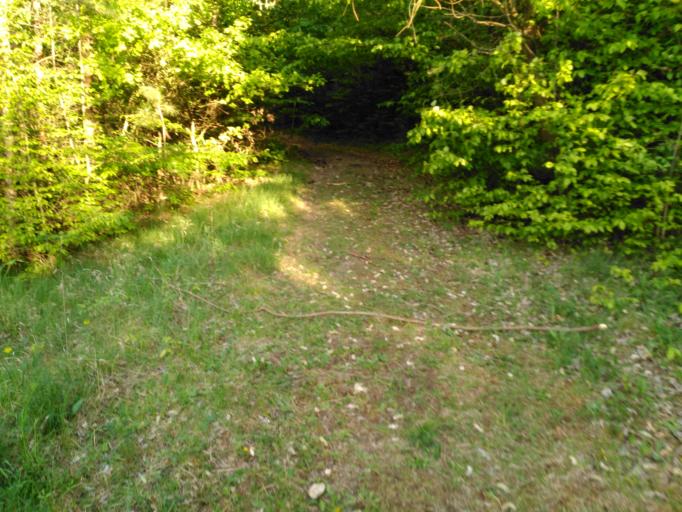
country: CZ
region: Central Bohemia
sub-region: Okres Beroun
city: Kraluv Dvur
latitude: 49.9185
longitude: 14.0656
